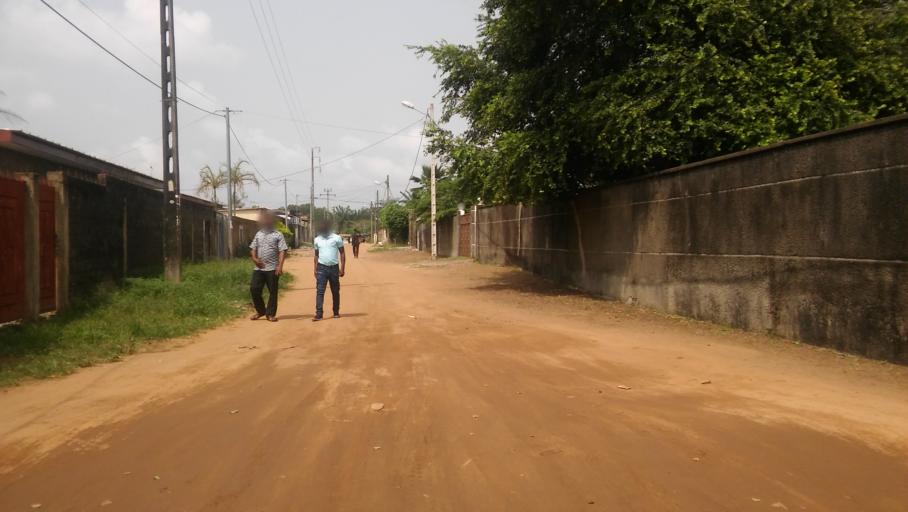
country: CI
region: Sud-Comoe
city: Grand-Bassam
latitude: 5.2178
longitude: -3.7290
